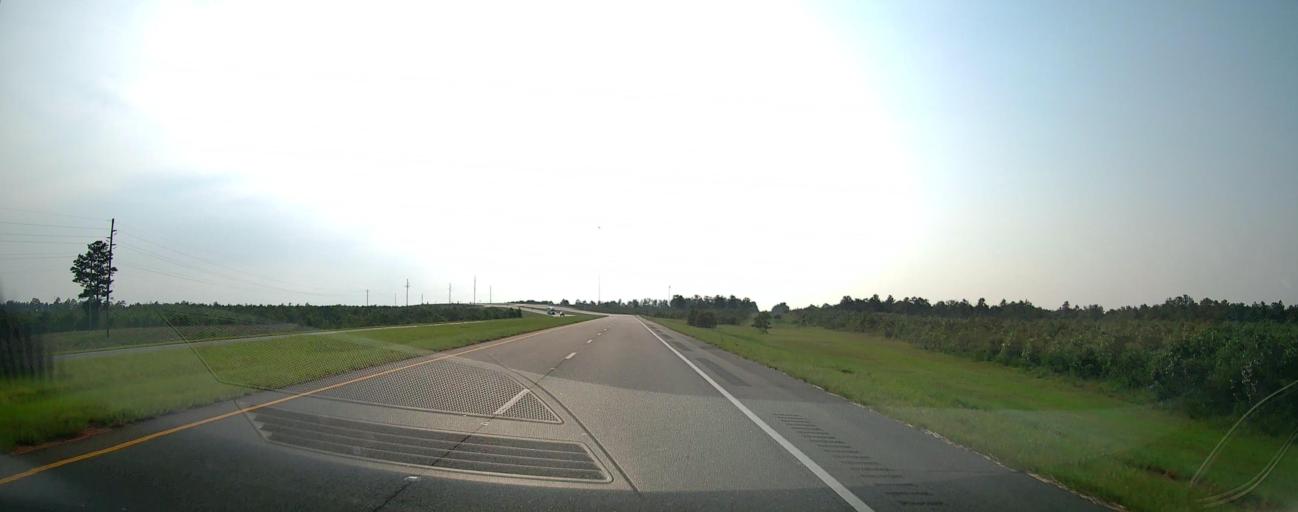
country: US
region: Georgia
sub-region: Talbot County
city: Talbotton
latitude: 32.5964
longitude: -84.4437
